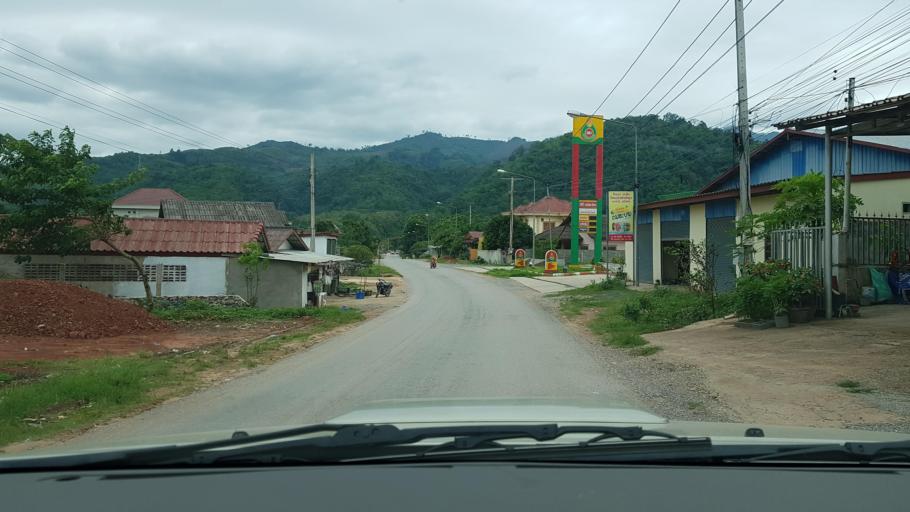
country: LA
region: Oudomxai
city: Muang Xay
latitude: 20.6994
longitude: 101.9995
